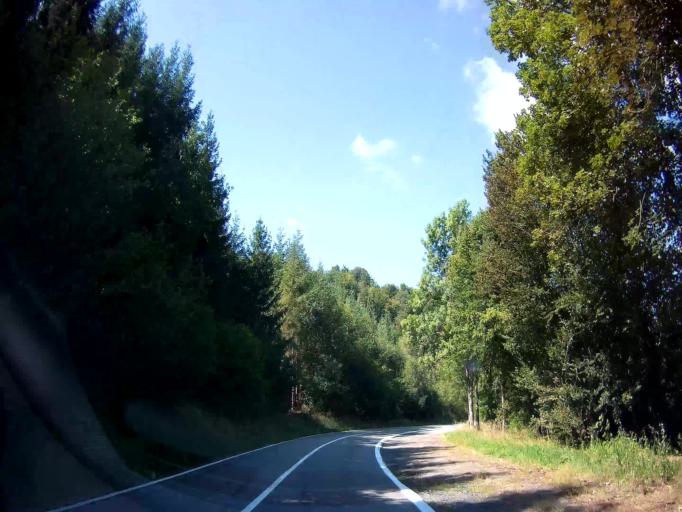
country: BE
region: Wallonia
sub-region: Province du Luxembourg
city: Bertogne
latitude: 50.0980
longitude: 5.6754
